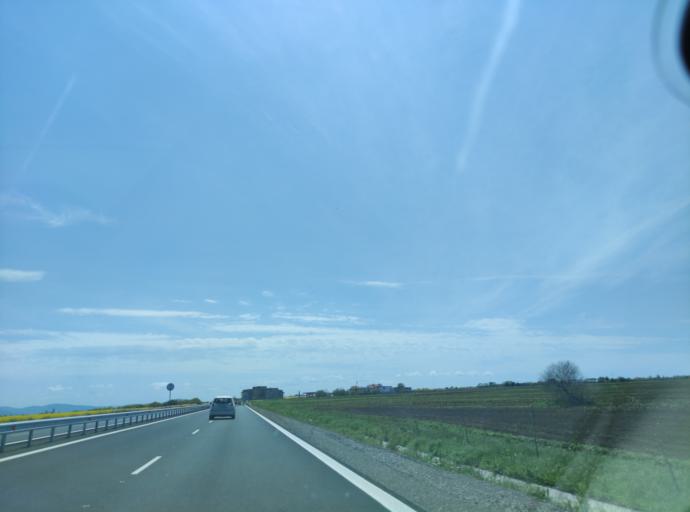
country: BG
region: Burgas
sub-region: Obshtina Pomorie
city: Pomorie
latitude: 42.5663
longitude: 27.5721
